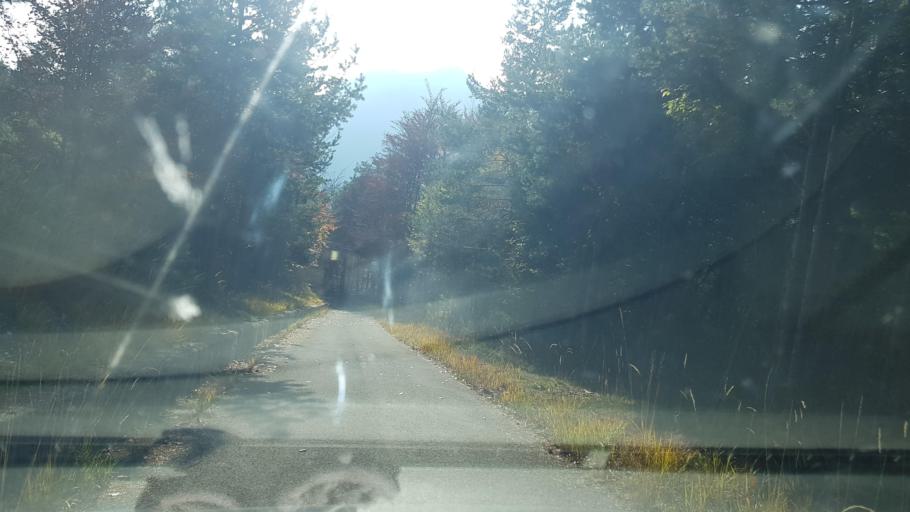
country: IT
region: Friuli Venezia Giulia
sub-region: Provincia di Udine
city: Moggio Udinese
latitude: 46.4526
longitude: 13.2030
